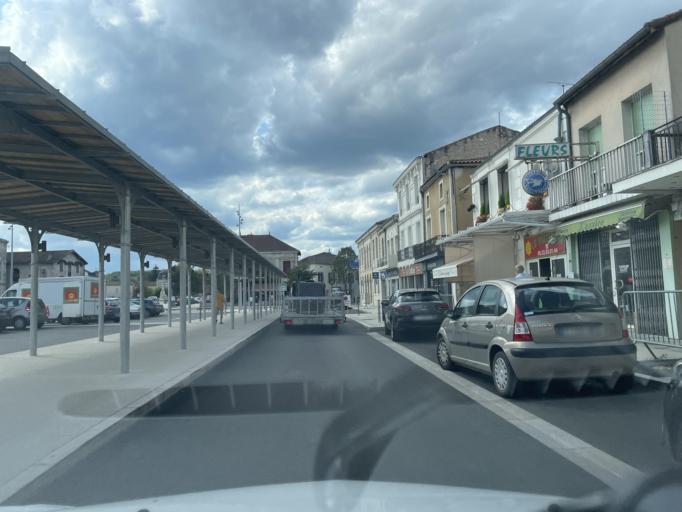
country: FR
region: Aquitaine
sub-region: Departement du Lot-et-Garonne
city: Casteljaloux
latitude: 44.3143
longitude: 0.0860
